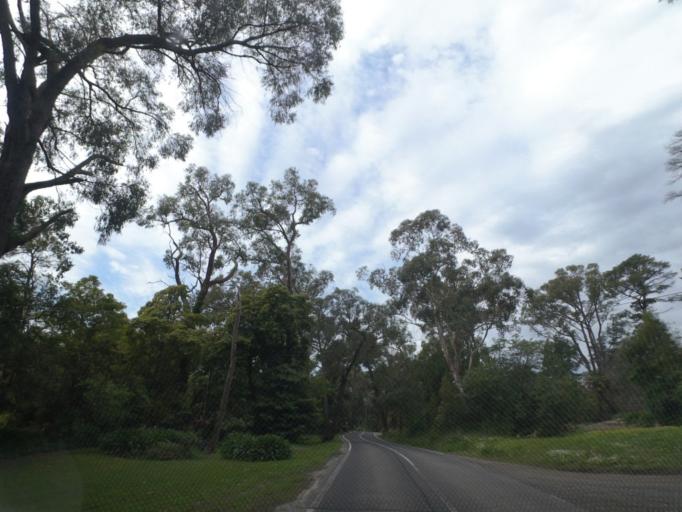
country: AU
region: Victoria
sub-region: Yarra Ranges
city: Montrose
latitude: -37.8171
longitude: 145.3484
